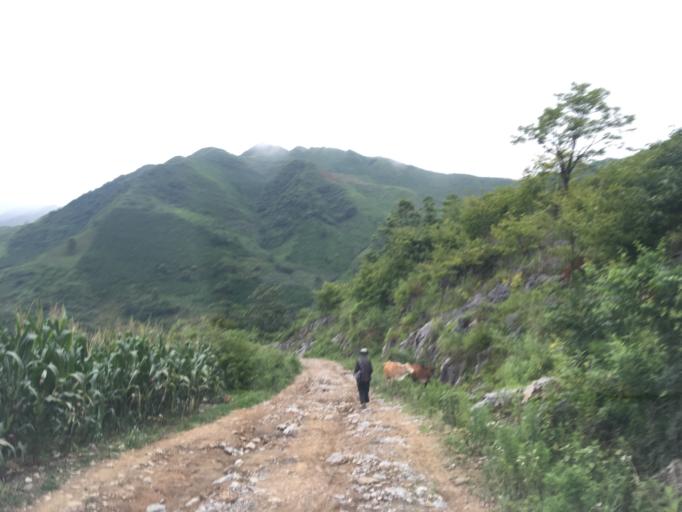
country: CN
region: Guangxi Zhuangzu Zizhiqu
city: Xinzhou
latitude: 24.9912
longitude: 105.6380
